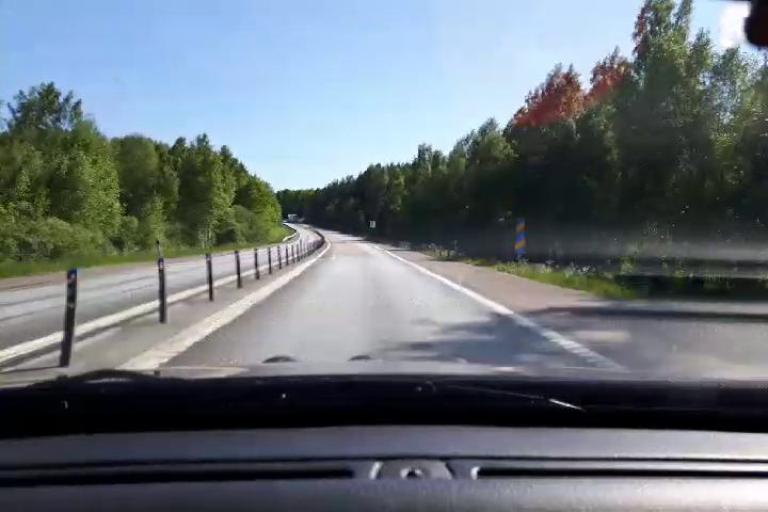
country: SE
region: Gaevleborg
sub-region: Soderhamns Kommun
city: Soderhamn
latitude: 61.2742
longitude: 17.0264
